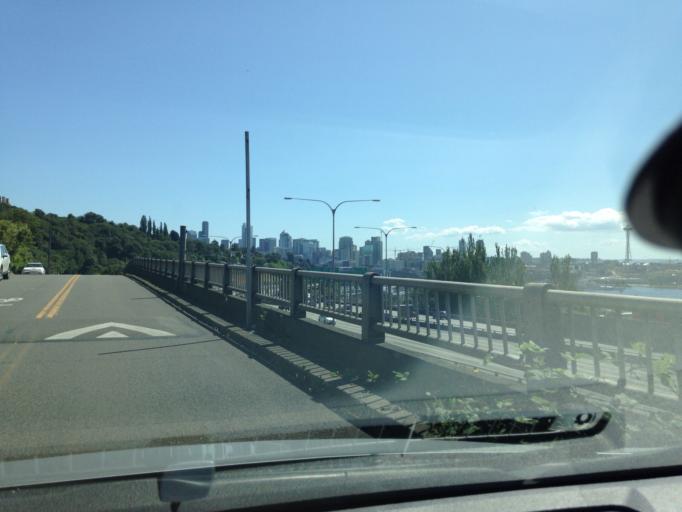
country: US
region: Washington
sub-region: King County
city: Seattle
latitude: 47.6380
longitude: -122.3224
